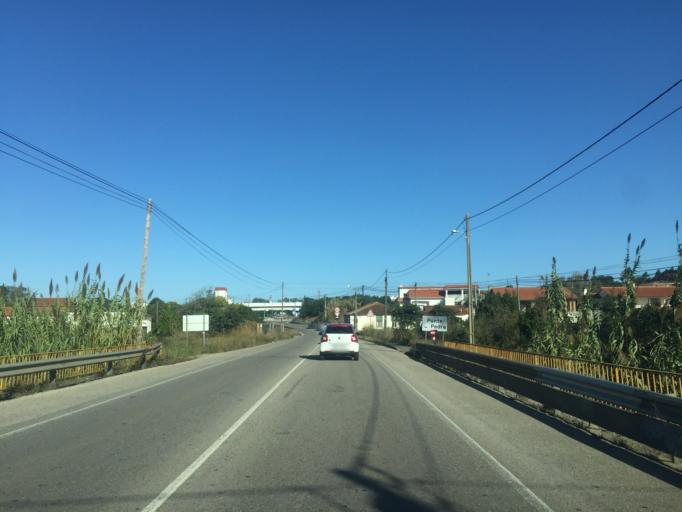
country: PT
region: Leiria
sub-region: Leiria
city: Amor
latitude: 39.7845
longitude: -8.8248
